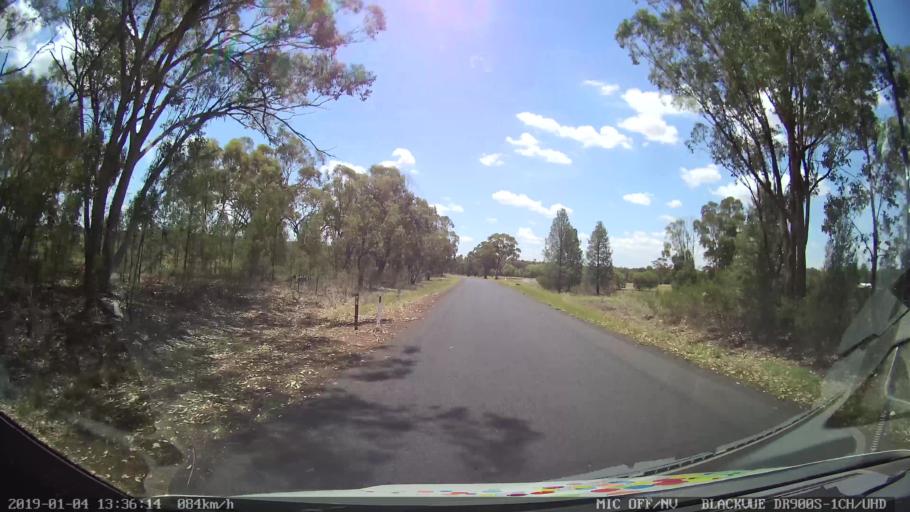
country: AU
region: New South Wales
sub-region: Dubbo Municipality
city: Dubbo
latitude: -32.5634
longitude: 148.5369
